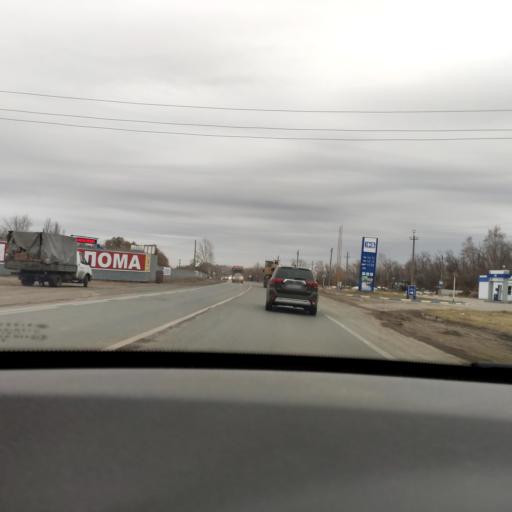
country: RU
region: Samara
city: Novokuybyshevsk
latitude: 53.0820
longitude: 50.0729
